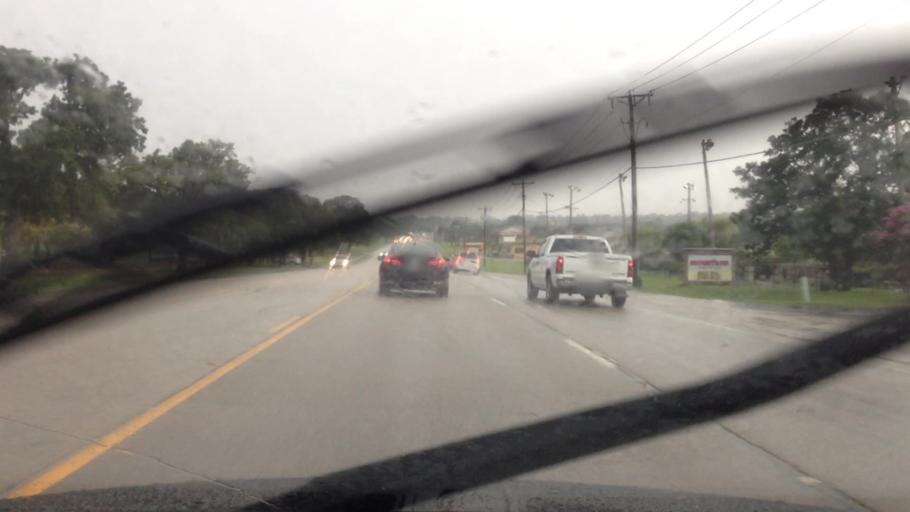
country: US
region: Texas
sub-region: Tarrant County
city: Hurst
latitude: 32.8484
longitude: -97.1952
